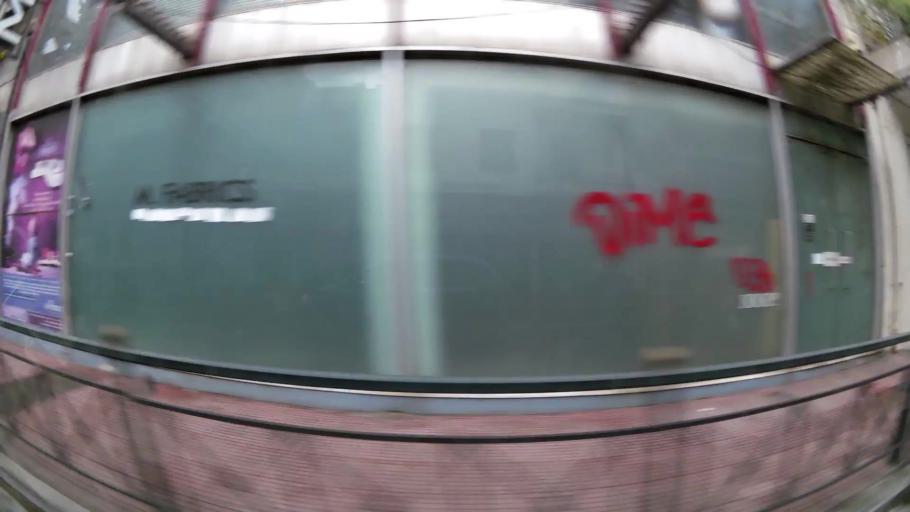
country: GR
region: Attica
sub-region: Nomarchia Athinas
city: Dhafni
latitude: 37.9593
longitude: 23.7376
